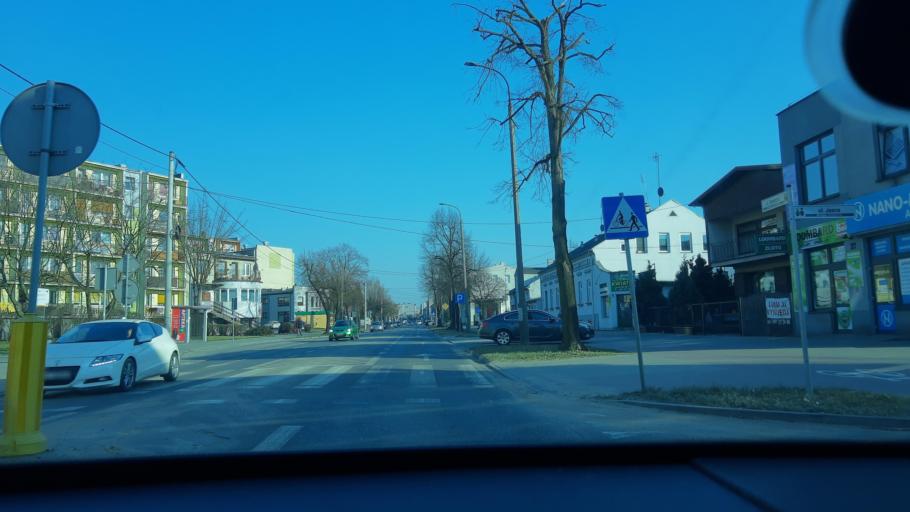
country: PL
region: Lodz Voivodeship
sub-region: Powiat zdunskowolski
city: Zdunska Wola
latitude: 51.6043
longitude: 18.9276
